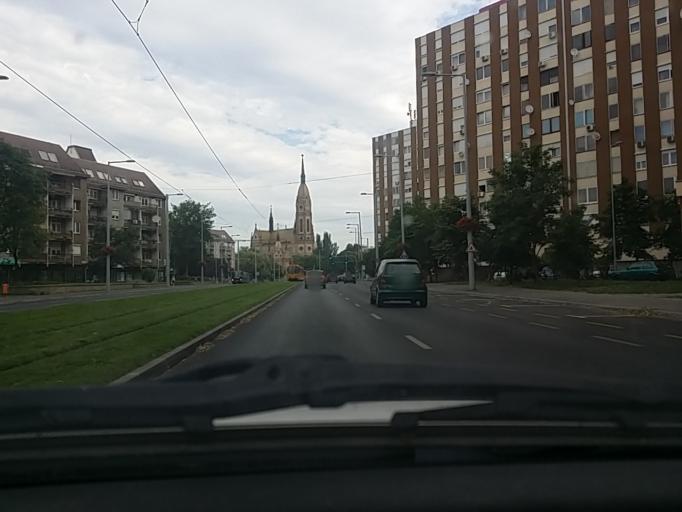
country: HU
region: Budapest
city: Budapest X. keruelet
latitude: 47.4837
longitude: 19.1314
